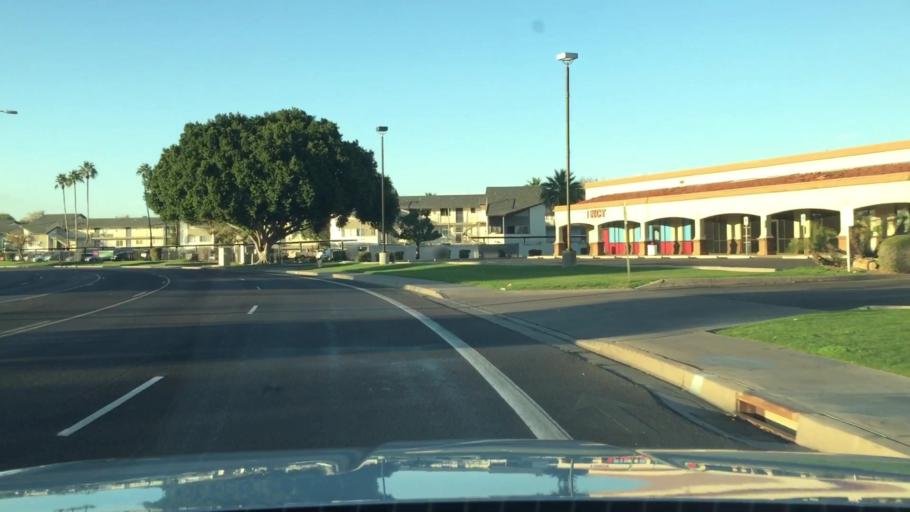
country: US
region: Arizona
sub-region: Maricopa County
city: Mesa
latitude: 33.3941
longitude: -111.8637
